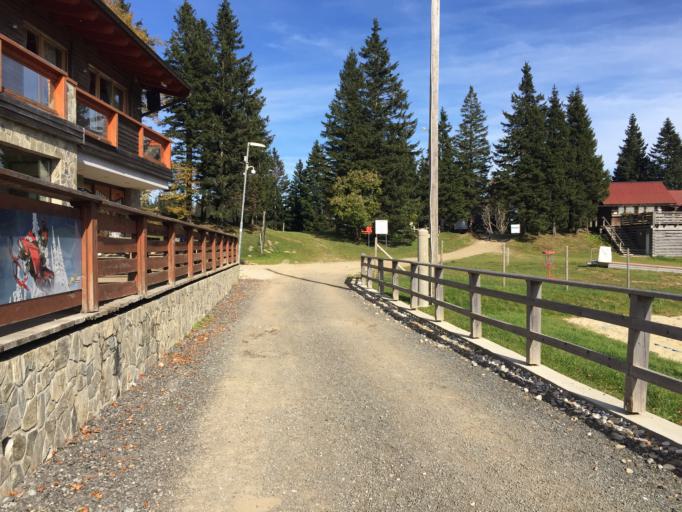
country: SI
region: Mislinja
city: Mislinja
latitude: 46.5027
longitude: 15.2107
